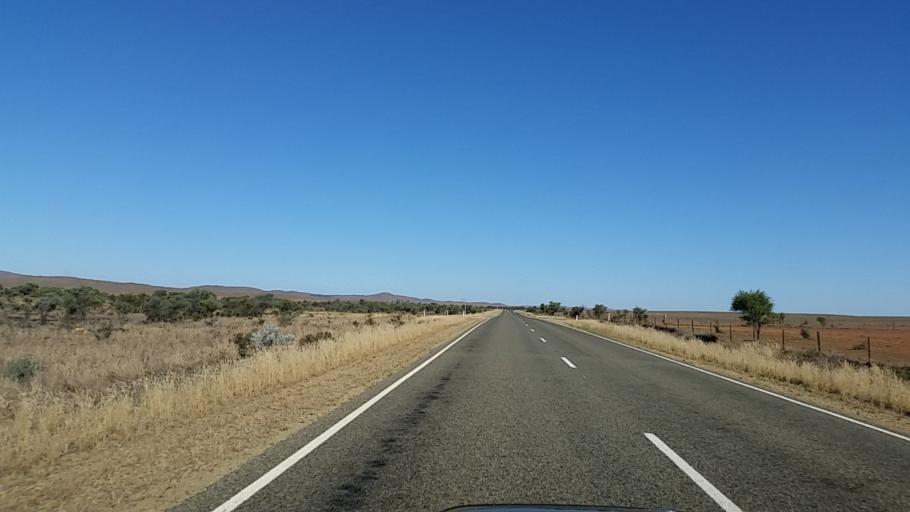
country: AU
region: South Australia
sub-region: Flinders Ranges
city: Quorn
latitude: -32.3980
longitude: 138.5125
